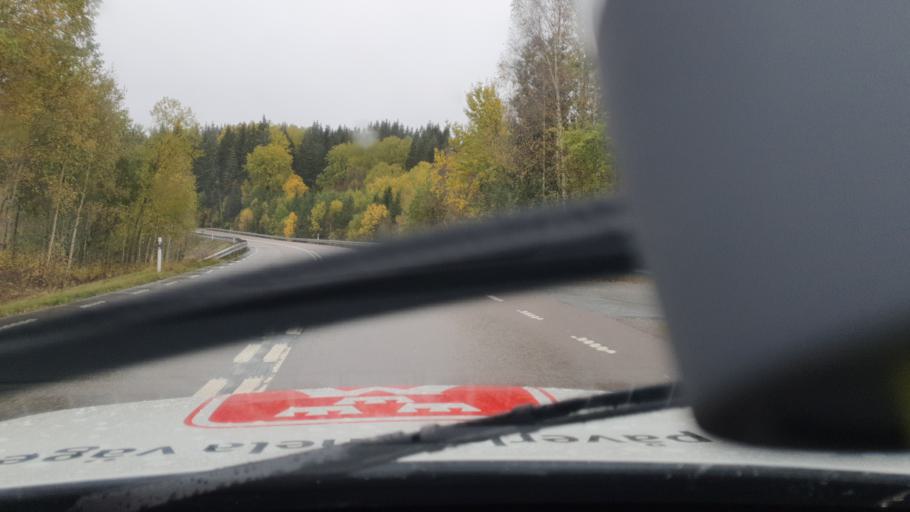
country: SE
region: Vaestra Goetaland
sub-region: Dals-Ed Kommun
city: Ed
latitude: 58.9347
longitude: 12.0473
